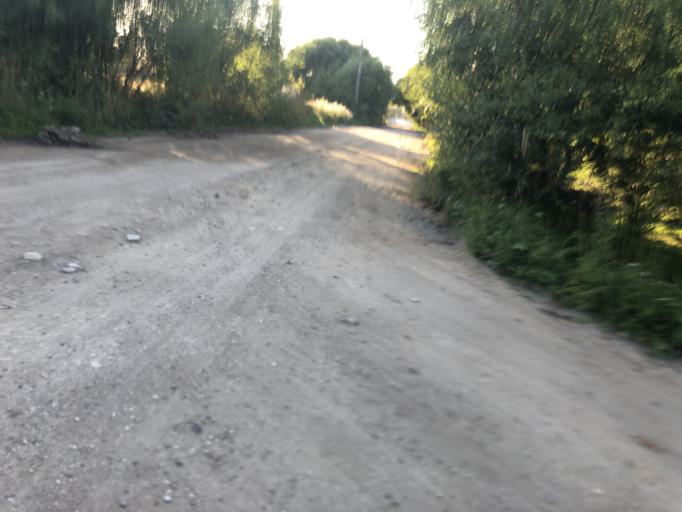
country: RU
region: Tverskaya
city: Rzhev
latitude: 56.2448
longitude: 34.3043
